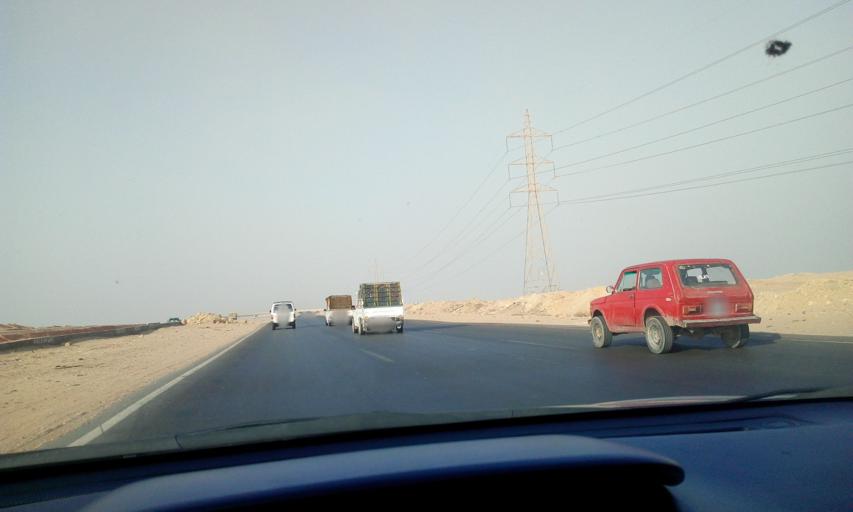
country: EG
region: Al Jizah
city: Madinat Sittah Uktubar
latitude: 29.9031
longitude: 31.0869
